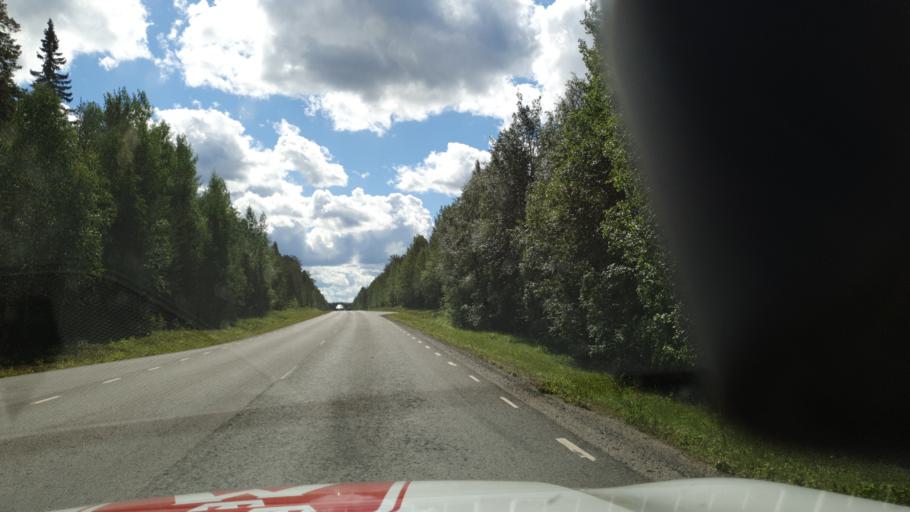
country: SE
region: Vaesterbotten
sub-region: Lycksele Kommun
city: Lycksele
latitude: 64.6191
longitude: 18.6876
